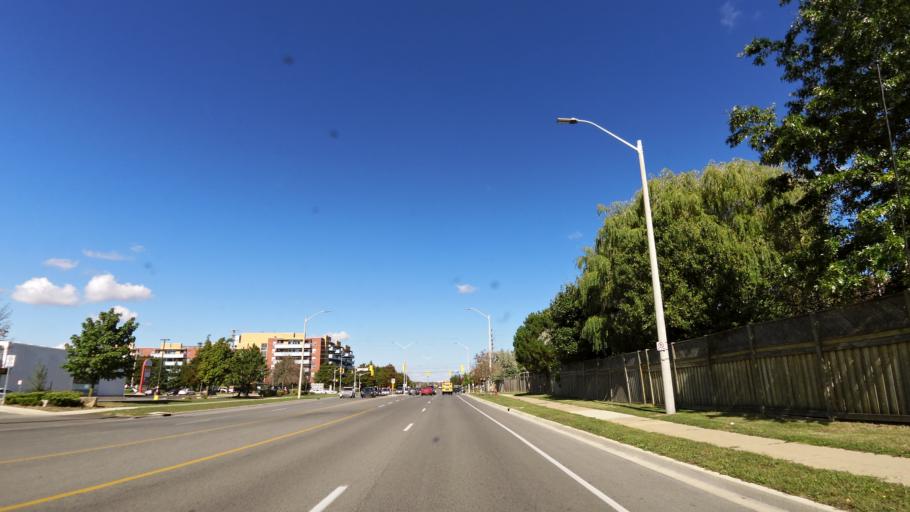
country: CA
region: Ontario
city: Mississauga
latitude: 43.5858
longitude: -79.6984
